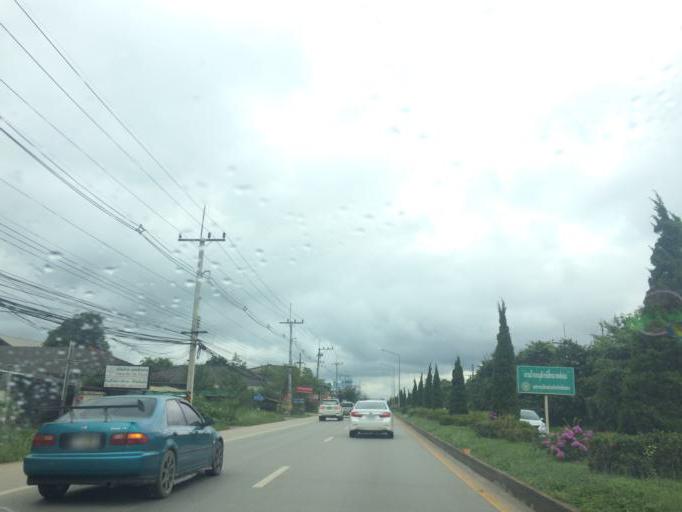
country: TH
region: Chiang Rai
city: Chiang Rai
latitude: 20.0077
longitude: 99.8679
